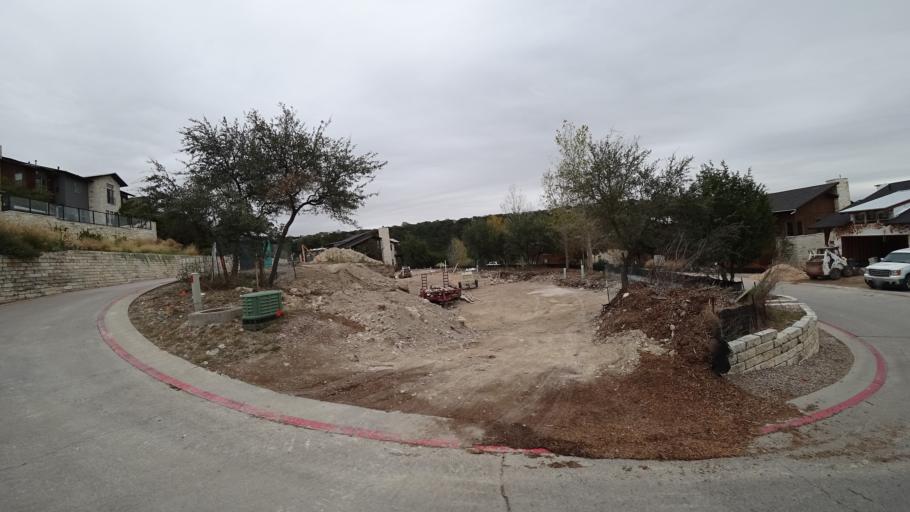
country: US
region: Texas
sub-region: Williamson County
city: Jollyville
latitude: 30.3810
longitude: -97.8061
